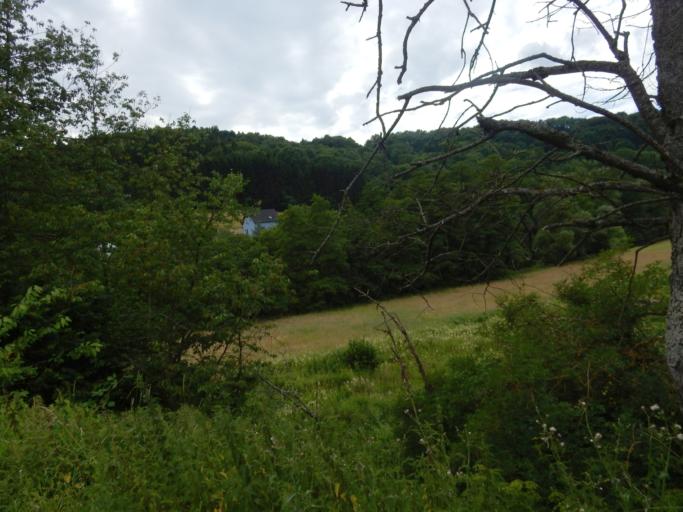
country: DE
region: Rheinland-Pfalz
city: Metterich
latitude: 49.9686
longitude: 6.5858
